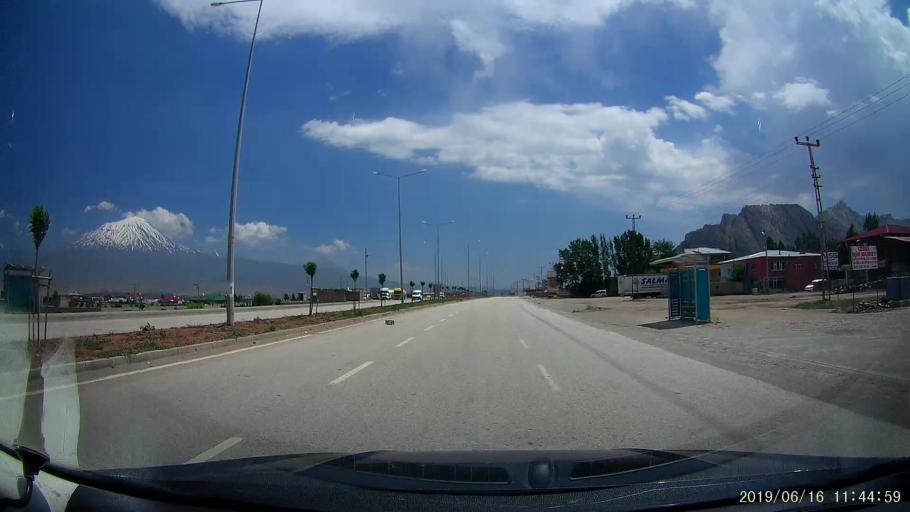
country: TR
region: Agri
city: Dogubayazit
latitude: 39.5574
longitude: 44.0962
